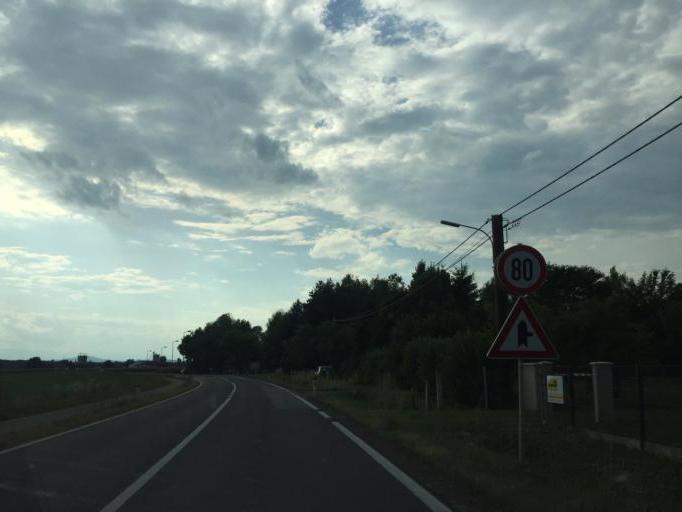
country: AT
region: Styria
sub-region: Politischer Bezirk Suedoststeiermark
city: Weinburg am Sassbach
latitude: 46.7569
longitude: 15.6832
